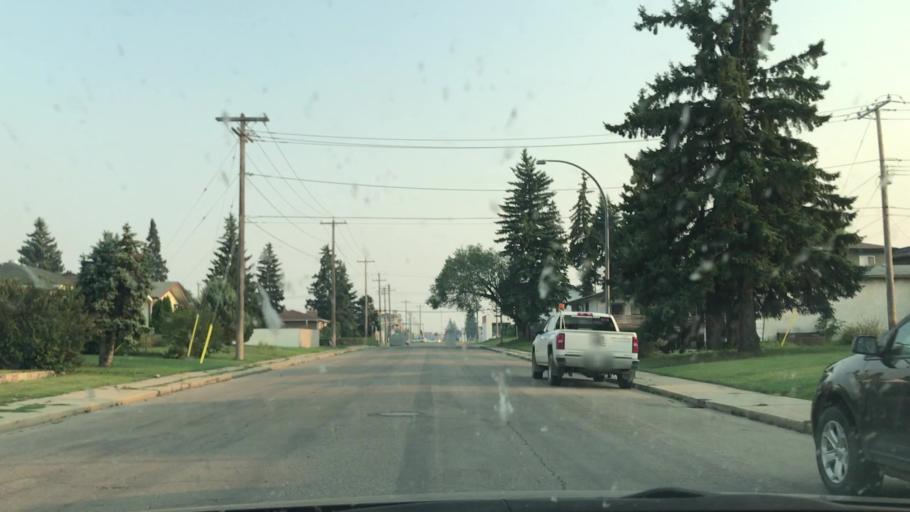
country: CA
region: Alberta
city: Edmonton
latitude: 53.5200
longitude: -113.4368
